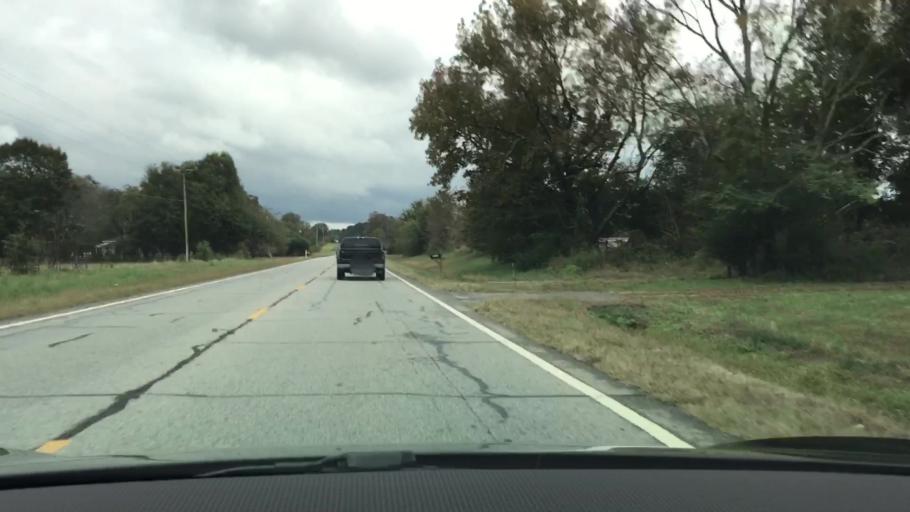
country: US
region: Georgia
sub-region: Oconee County
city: Watkinsville
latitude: 33.8220
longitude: -83.3683
